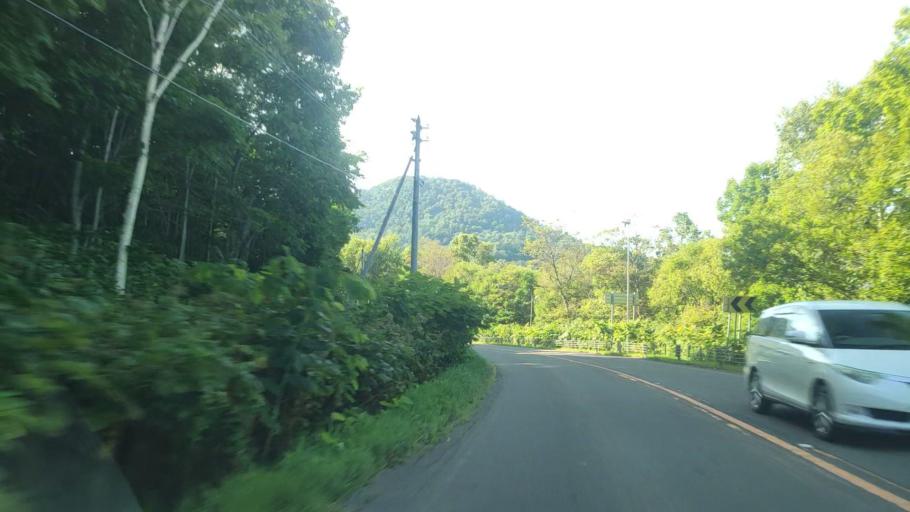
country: JP
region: Hokkaido
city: Nayoro
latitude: 44.7378
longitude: 142.1878
